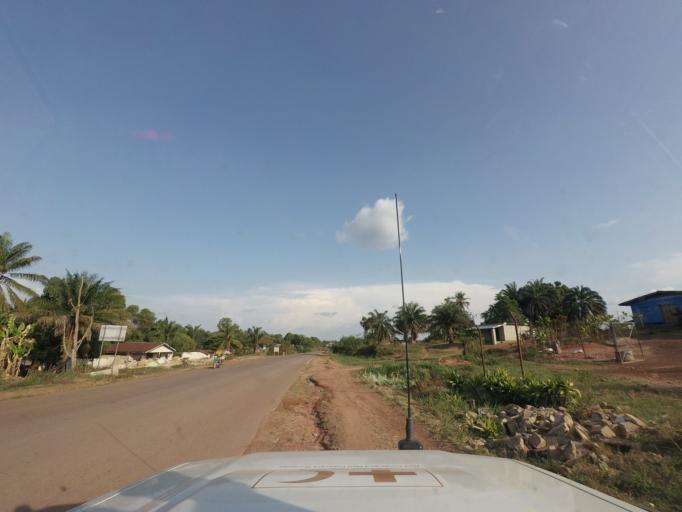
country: LR
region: Bong
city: Gbarnga
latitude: 7.0112
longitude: -9.4838
